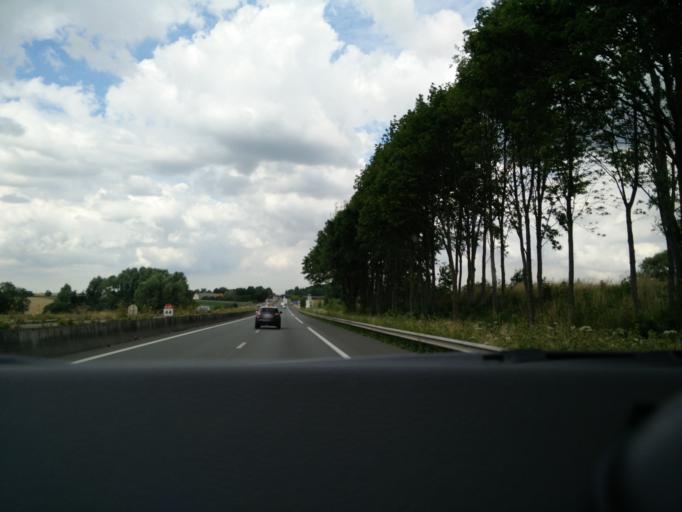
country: FR
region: Nord-Pas-de-Calais
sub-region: Departement du Nord
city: Steenvoorde
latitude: 50.8154
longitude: 2.5935
